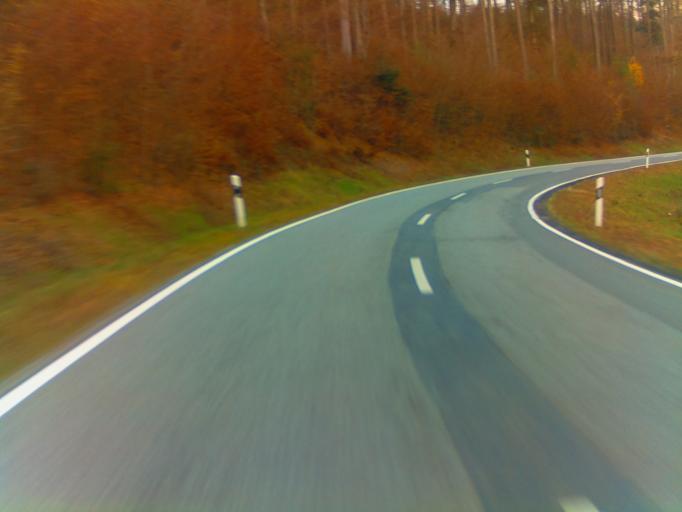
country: DE
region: Hesse
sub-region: Regierungsbezirk Darmstadt
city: Hesseneck
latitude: 49.5813
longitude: 9.0232
